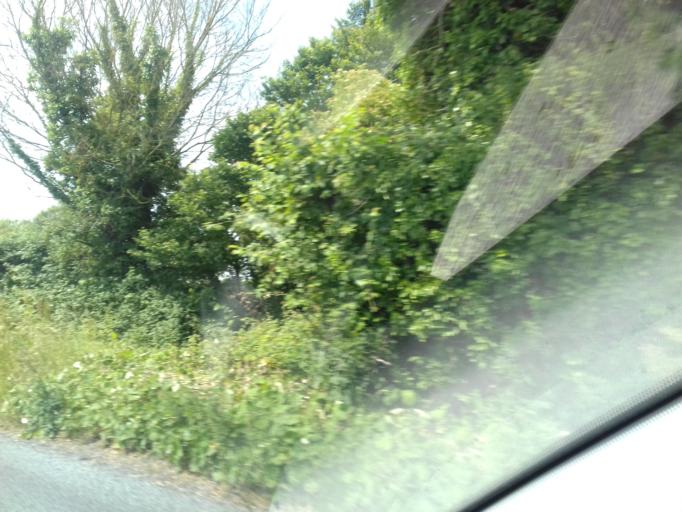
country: IE
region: Leinster
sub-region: An Mhi
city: Stamullin
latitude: 53.5572
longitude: -6.3135
